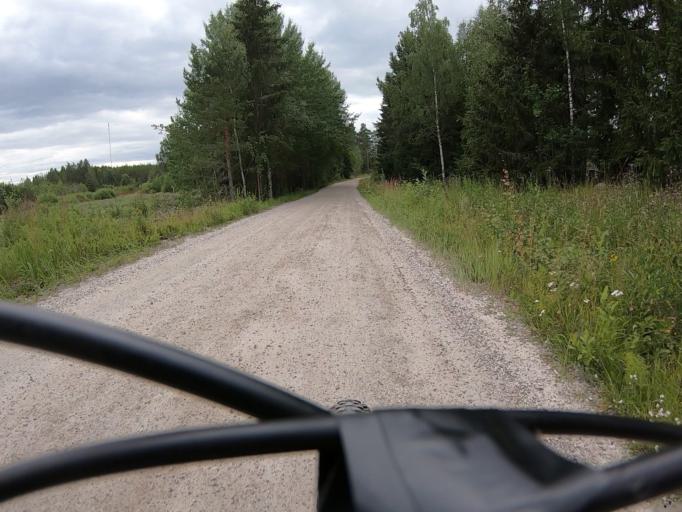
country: FI
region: Varsinais-Suomi
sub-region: Vakka-Suomi
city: Uusikaupunki
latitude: 60.8417
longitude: 21.3866
